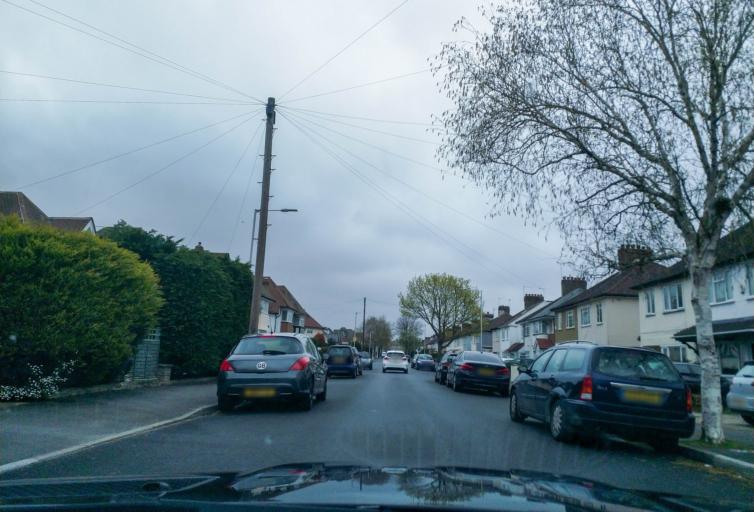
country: GB
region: England
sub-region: Greater London
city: Northolt
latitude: 51.5639
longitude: -0.3897
